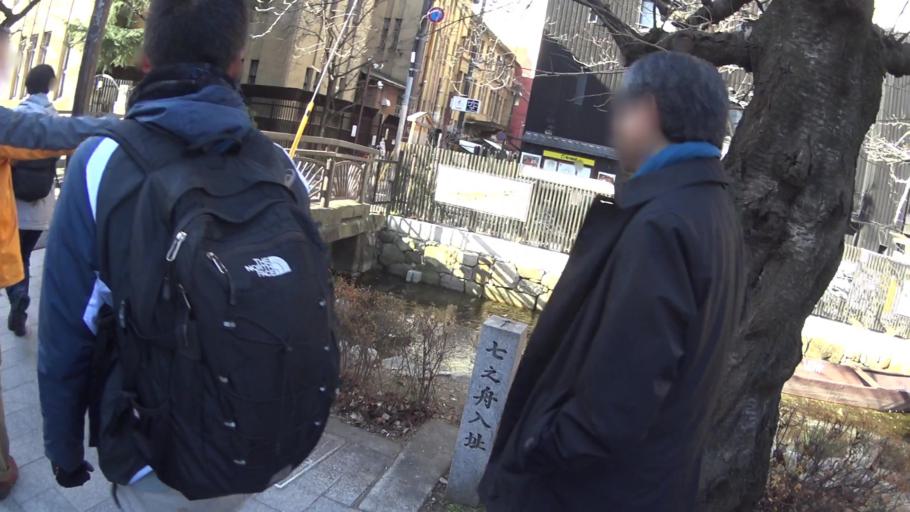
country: JP
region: Kyoto
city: Kyoto
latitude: 35.0046
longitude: 135.7712
